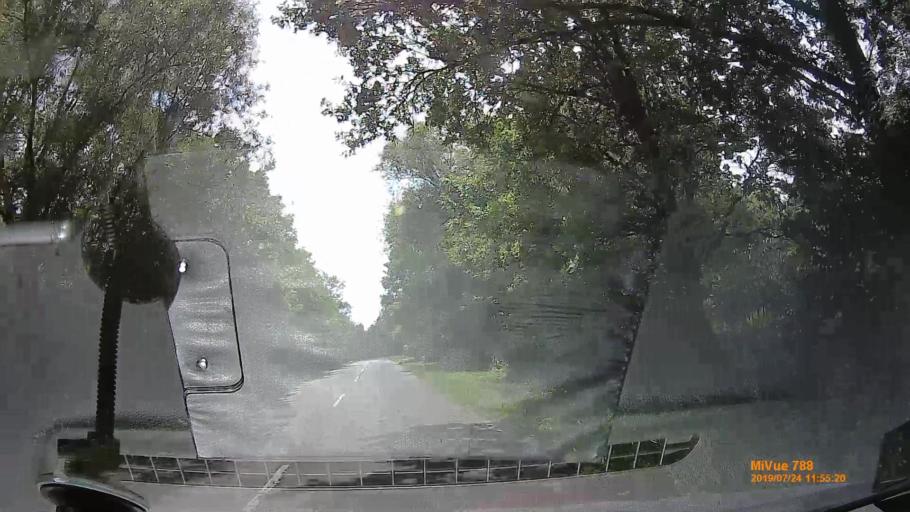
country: HU
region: Szabolcs-Szatmar-Bereg
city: Vasarosnameny
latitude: 48.2099
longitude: 22.4139
